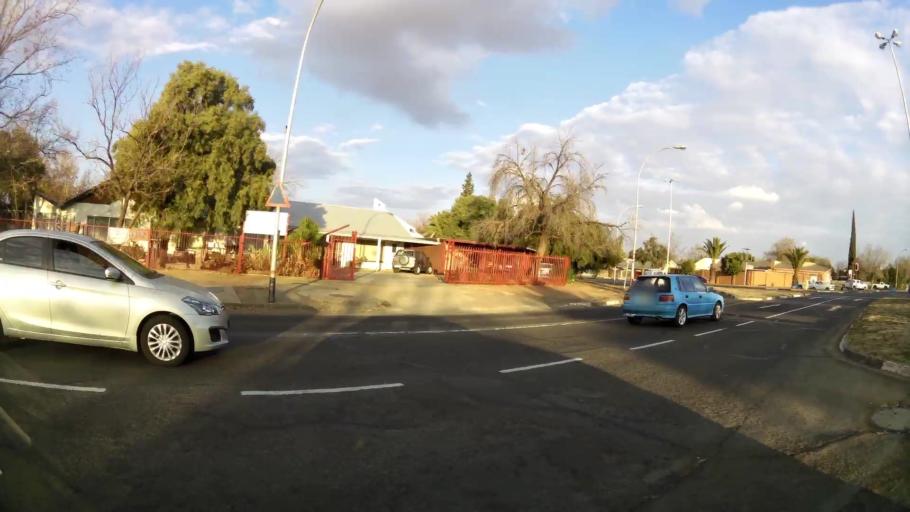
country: ZA
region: Orange Free State
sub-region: Mangaung Metropolitan Municipality
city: Bloemfontein
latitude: -29.1428
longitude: 26.1838
